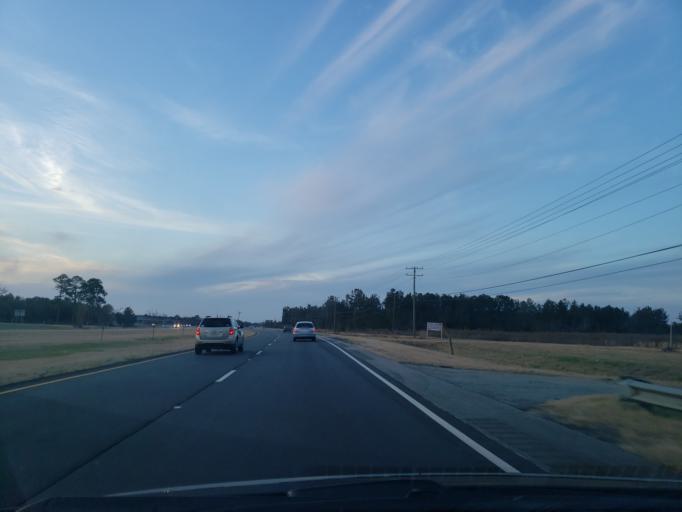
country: US
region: Georgia
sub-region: Dougherty County
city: Albany
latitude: 31.5706
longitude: -84.0238
